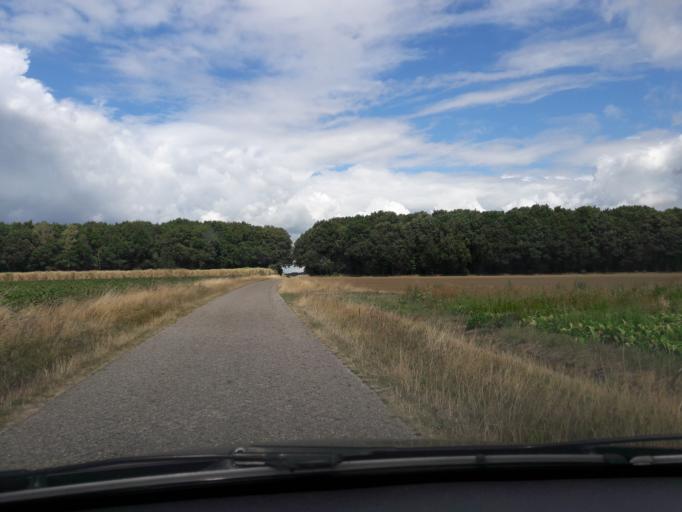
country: NL
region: Drenthe
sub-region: Gemeente Borger-Odoorn
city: Borger
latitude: 52.9348
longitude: 6.7947
